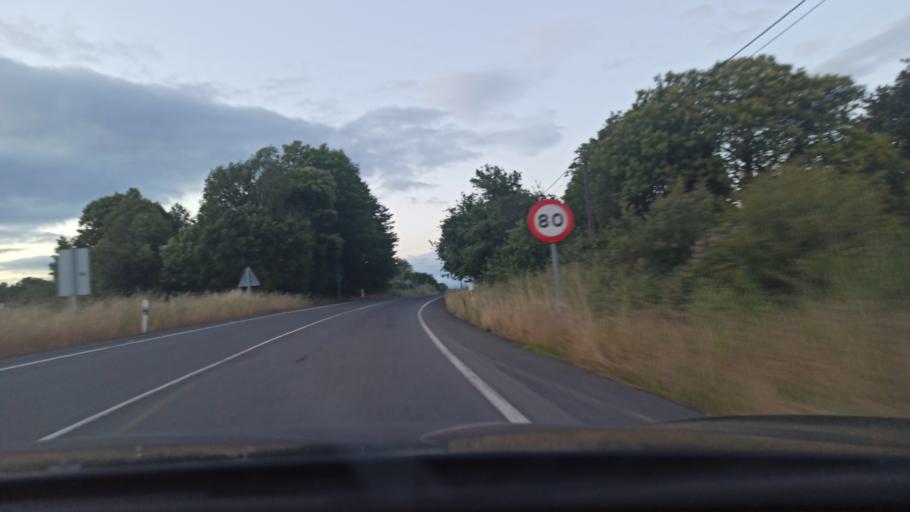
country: ES
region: Galicia
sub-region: Provincia de Lugo
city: Ourol
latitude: 42.9400
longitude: -7.6297
